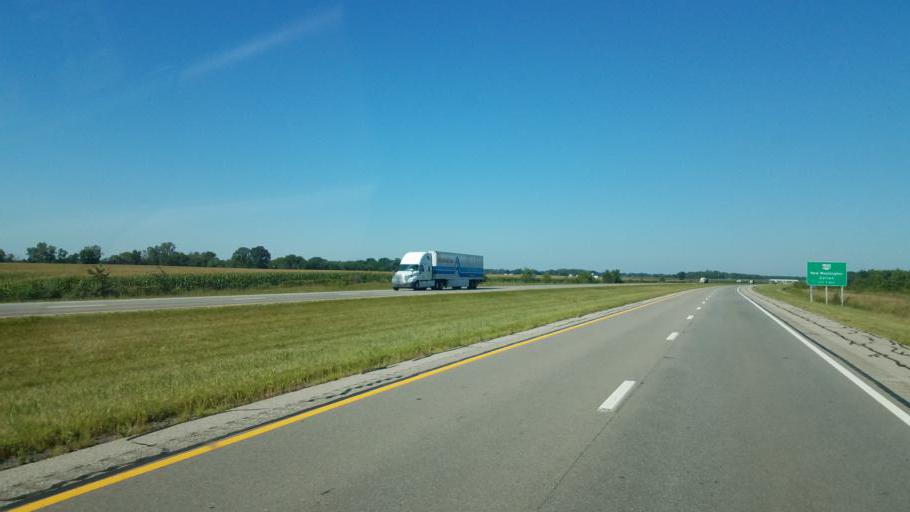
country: US
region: Ohio
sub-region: Crawford County
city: Galion
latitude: 40.7619
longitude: -82.8294
